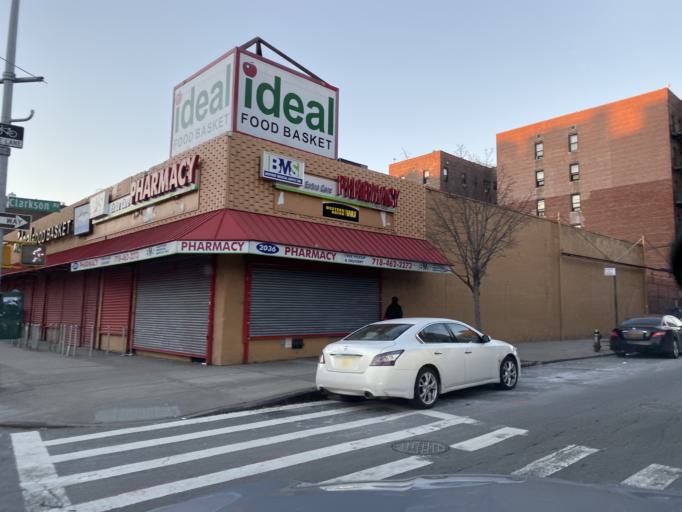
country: US
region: New York
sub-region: Kings County
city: Brooklyn
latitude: 40.6551
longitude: -73.9563
